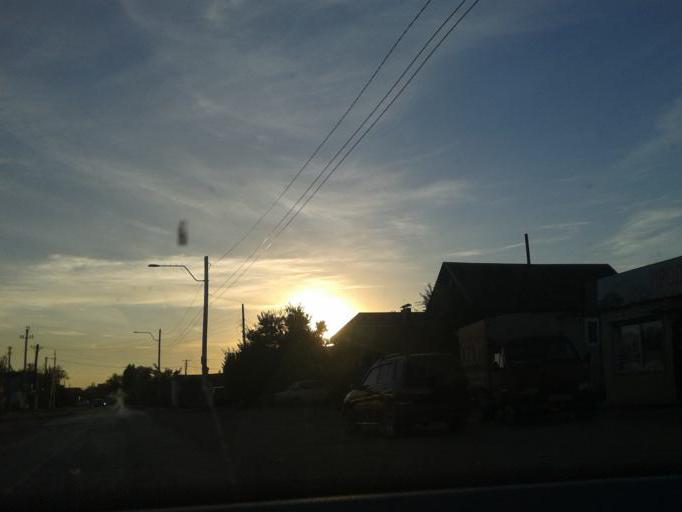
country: RU
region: Volgograd
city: Krasnoslobodsk
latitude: 48.7033
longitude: 44.5648
